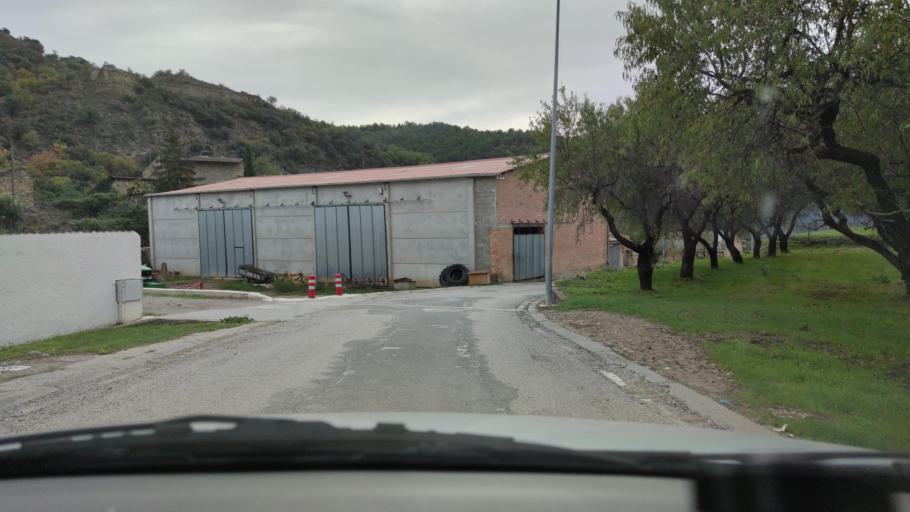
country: ES
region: Catalonia
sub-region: Provincia de Lleida
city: Llimiana
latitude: 42.0758
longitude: 0.9168
